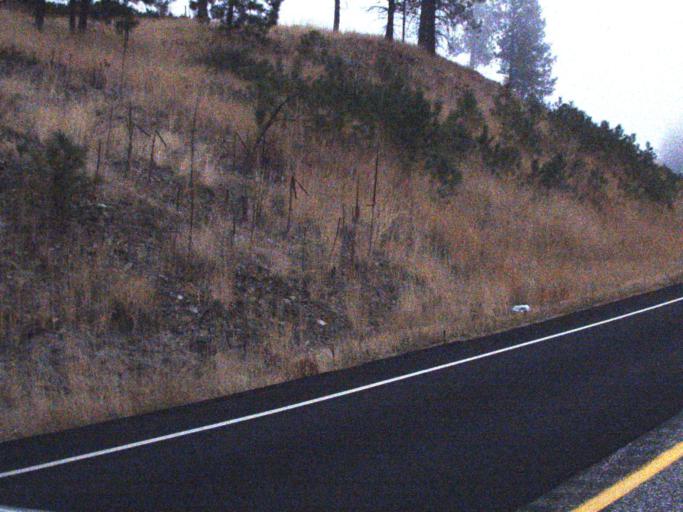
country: US
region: Washington
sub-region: Stevens County
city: Kettle Falls
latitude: 48.6962
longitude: -118.1250
